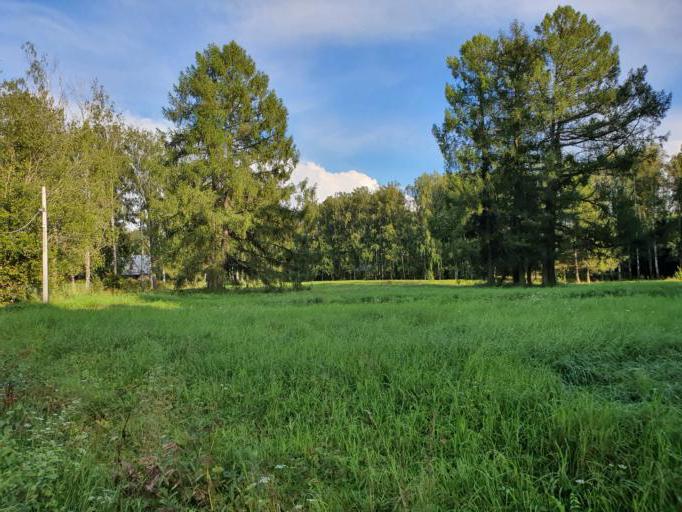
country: RU
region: St.-Petersburg
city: Tyarlevo
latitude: 59.6990
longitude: 30.4526
